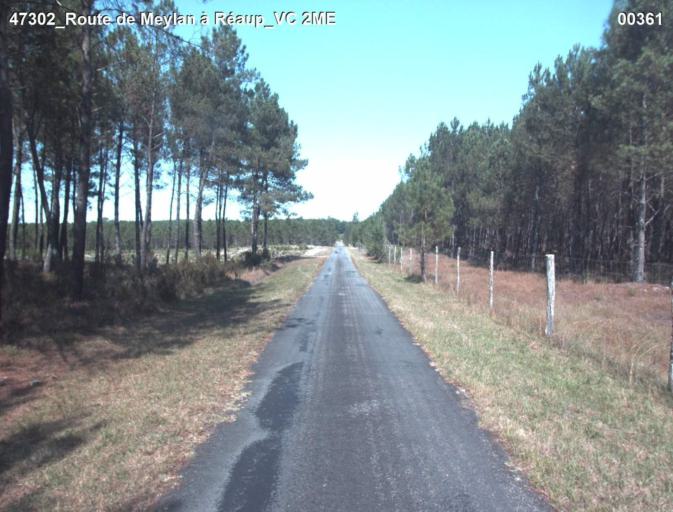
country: FR
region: Aquitaine
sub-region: Departement du Lot-et-Garonne
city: Mezin
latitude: 44.1048
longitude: 0.1388
